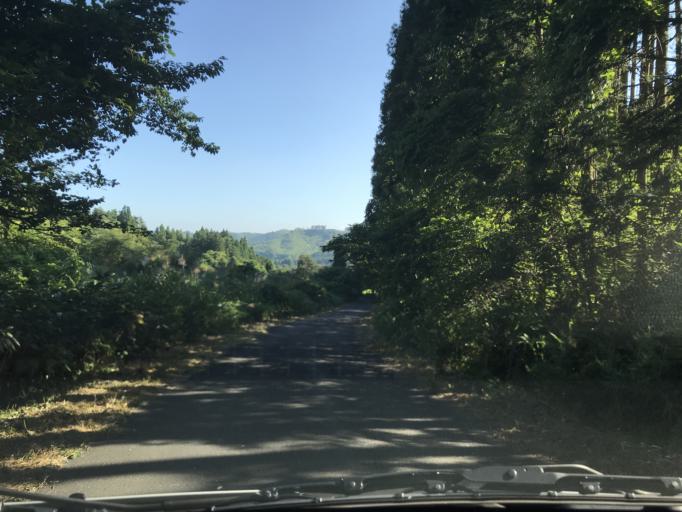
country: JP
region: Iwate
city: Mizusawa
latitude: 39.0615
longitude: 141.0409
